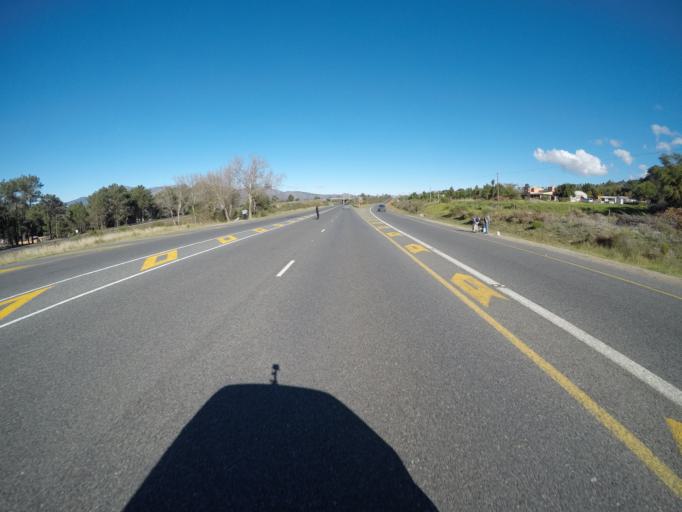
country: ZA
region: Western Cape
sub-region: Overberg District Municipality
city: Grabouw
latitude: -34.2273
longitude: 19.1877
